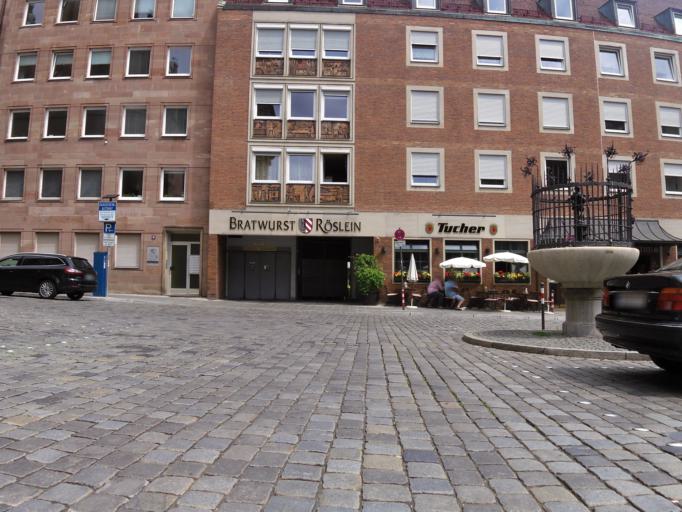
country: DE
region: Bavaria
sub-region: Regierungsbezirk Mittelfranken
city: Nuernberg
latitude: 49.4545
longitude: 11.0774
